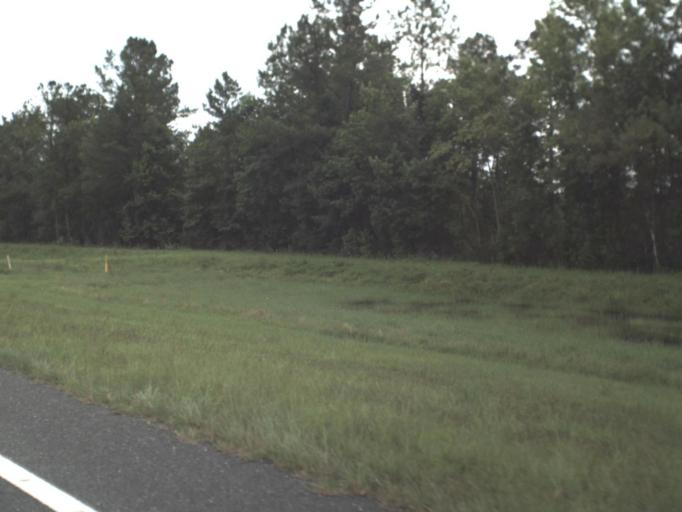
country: US
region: Florida
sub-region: Levy County
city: Chiefland
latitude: 29.3339
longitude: -82.7724
